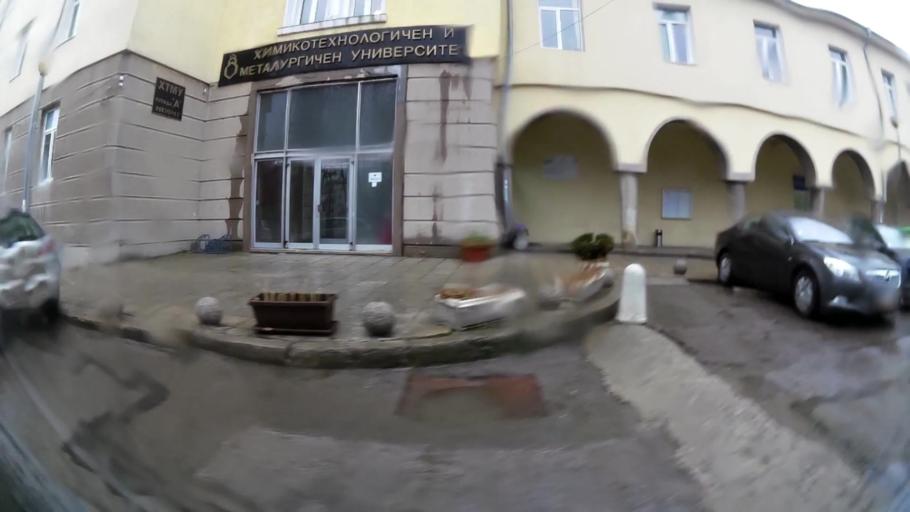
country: BG
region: Sofia-Capital
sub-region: Stolichna Obshtina
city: Sofia
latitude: 42.6555
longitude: 23.3585
